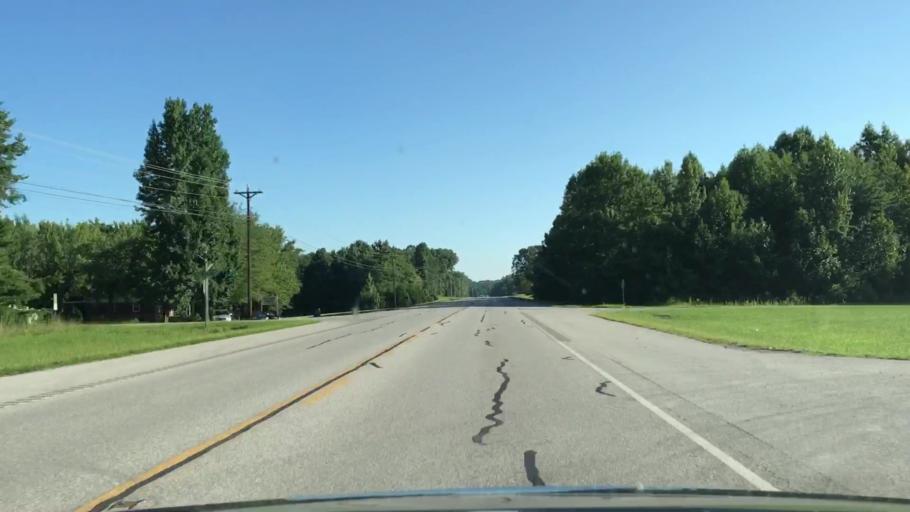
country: US
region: Tennessee
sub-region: Putnam County
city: Baxter
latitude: 36.1960
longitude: -85.6172
